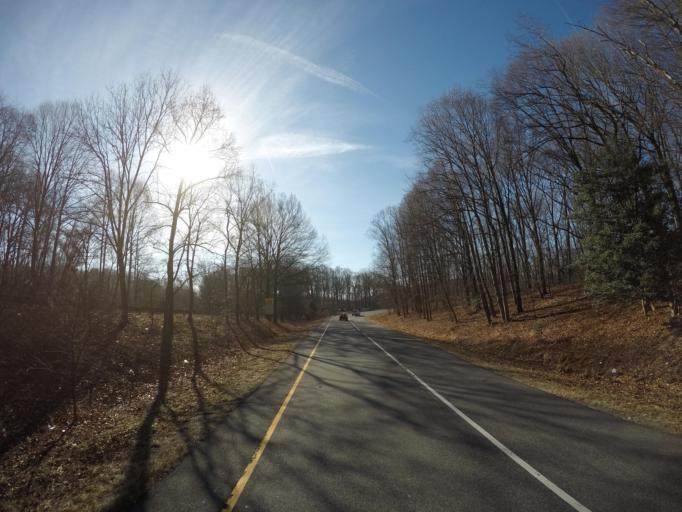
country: US
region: Maryland
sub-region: Howard County
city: Savage
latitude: 39.1593
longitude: -76.8323
